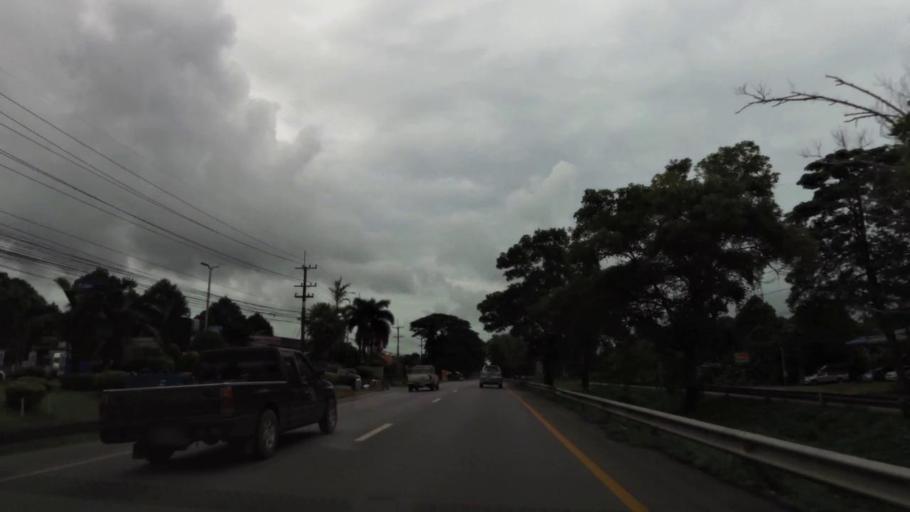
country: TH
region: Chanthaburi
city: Tha Mai
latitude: 12.6489
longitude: 102.0278
